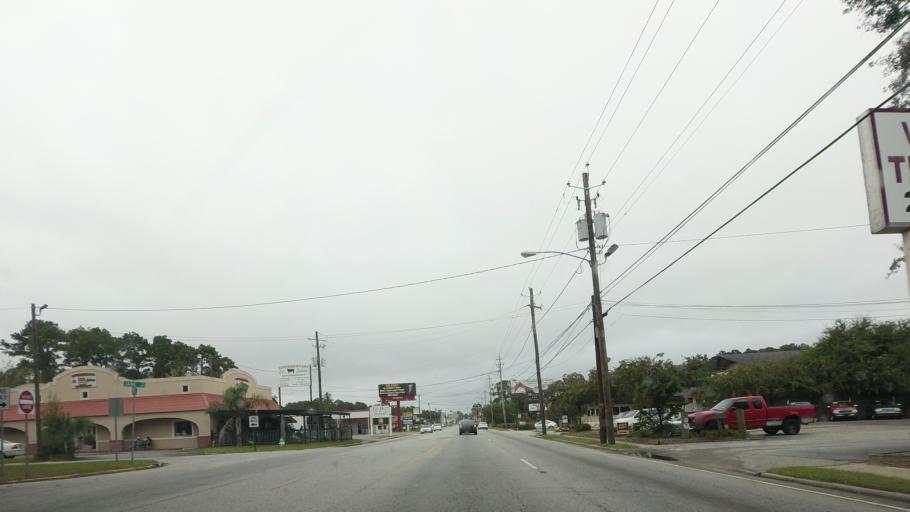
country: US
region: Georgia
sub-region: Lowndes County
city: Valdosta
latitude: 30.8463
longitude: -83.2804
